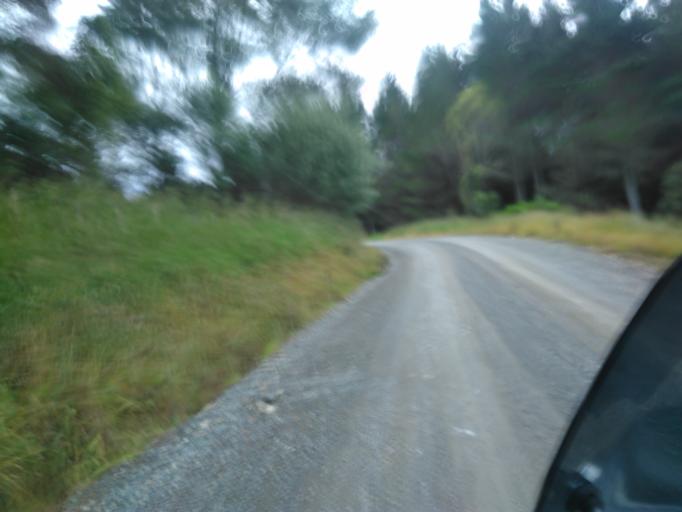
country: NZ
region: Gisborne
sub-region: Gisborne District
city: Gisborne
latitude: -38.0485
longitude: 178.1239
